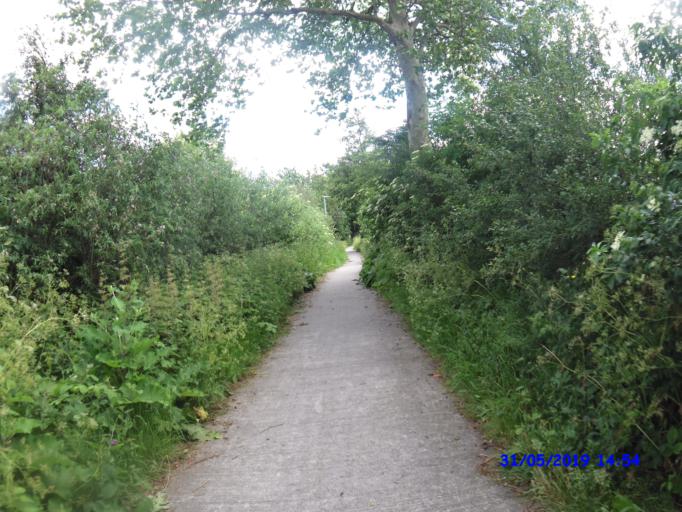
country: FR
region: Nord-Pas-de-Calais
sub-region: Departement du Nord
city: Comines
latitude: 50.7836
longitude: 2.9700
